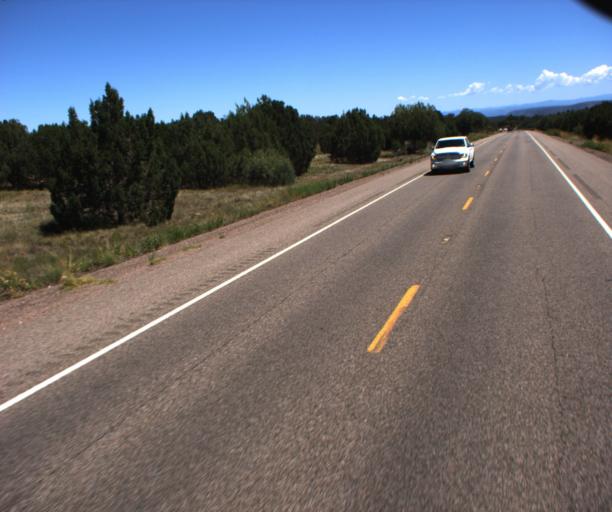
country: US
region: Arizona
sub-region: Navajo County
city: Cibecue
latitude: 33.6973
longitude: -110.5518
